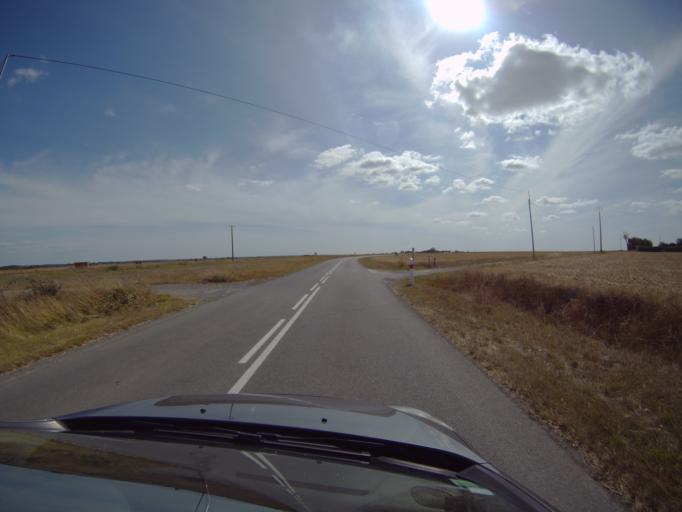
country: FR
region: Poitou-Charentes
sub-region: Departement des Deux-Sevres
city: Saint-Hilaire-la-Palud
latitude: 46.2697
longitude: -0.6648
